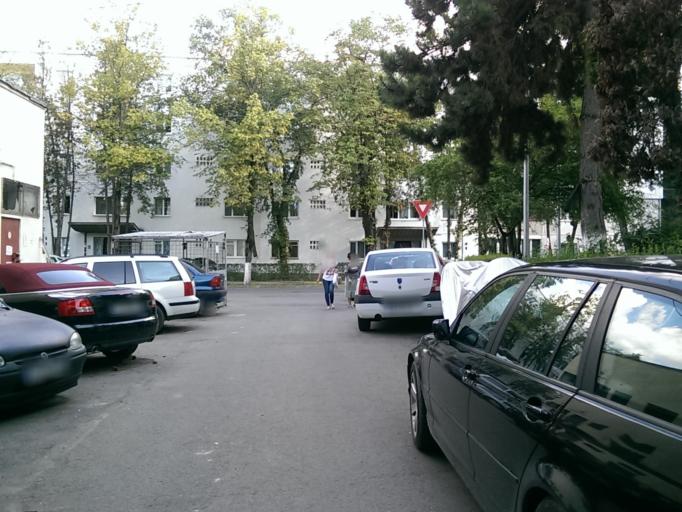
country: RO
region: Cluj
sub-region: Municipiul Cluj-Napoca
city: Cluj-Napoca
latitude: 46.7639
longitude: 23.6160
